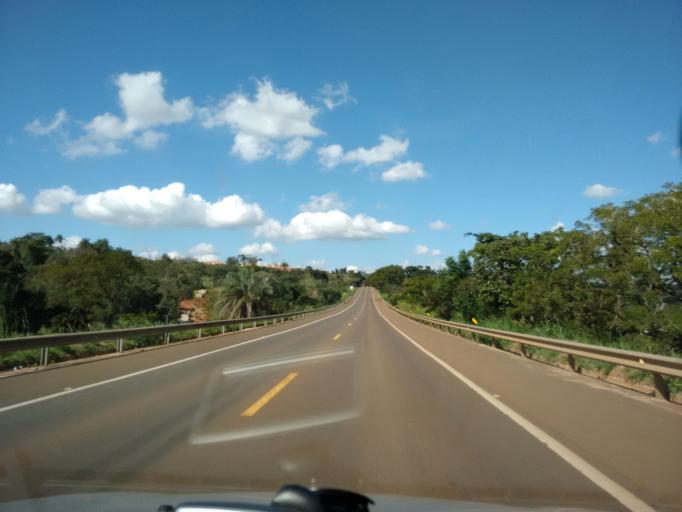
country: BR
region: Sao Paulo
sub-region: Sao Carlos
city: Sao Carlos
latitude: -22.0662
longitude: -47.9142
